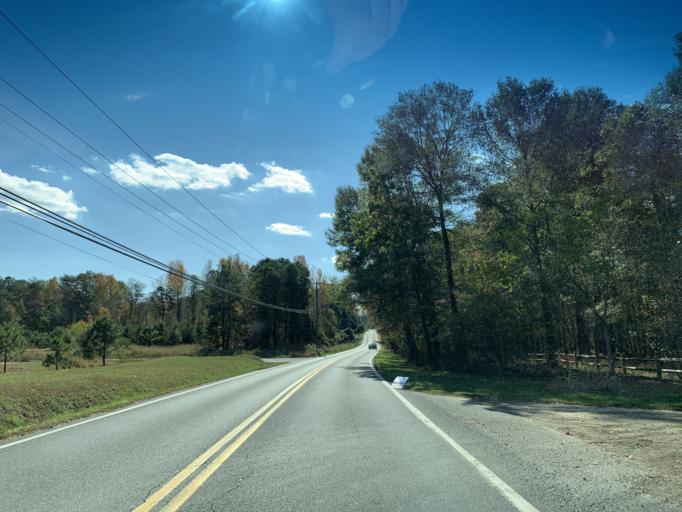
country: US
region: Maryland
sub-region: Anne Arundel County
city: Gambrills
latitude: 39.0980
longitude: -76.6531
